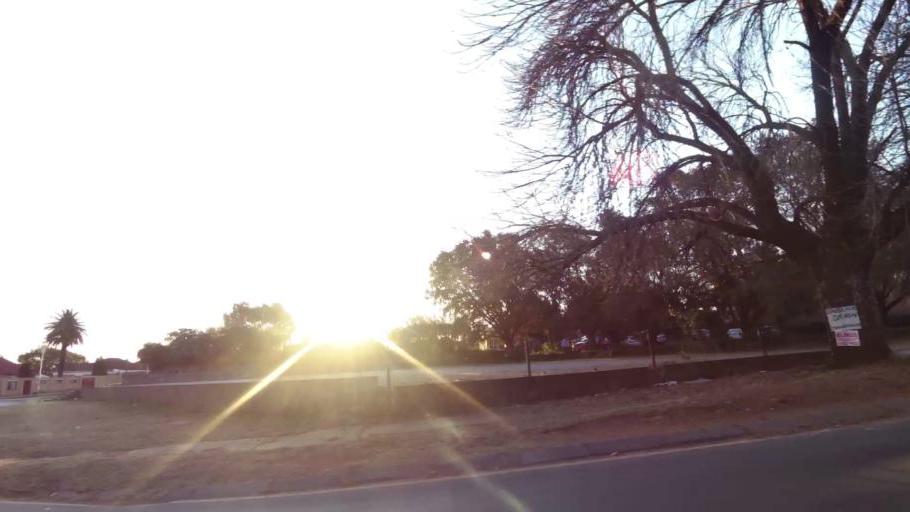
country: ZA
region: Gauteng
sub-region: City of Johannesburg Metropolitan Municipality
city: Roodepoort
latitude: -26.1812
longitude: 27.9412
